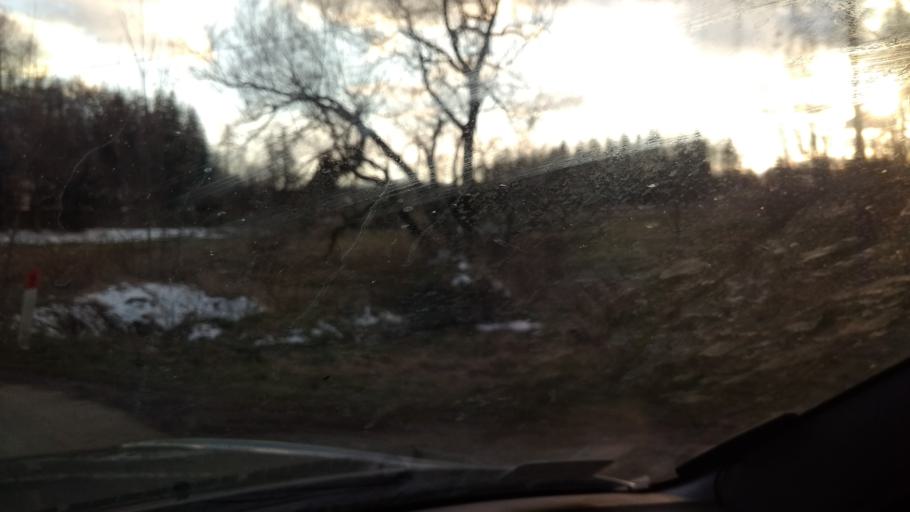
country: PL
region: Lower Silesian Voivodeship
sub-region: Powiat jeleniogorski
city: Sosnowka
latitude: 50.8427
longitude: 15.7388
